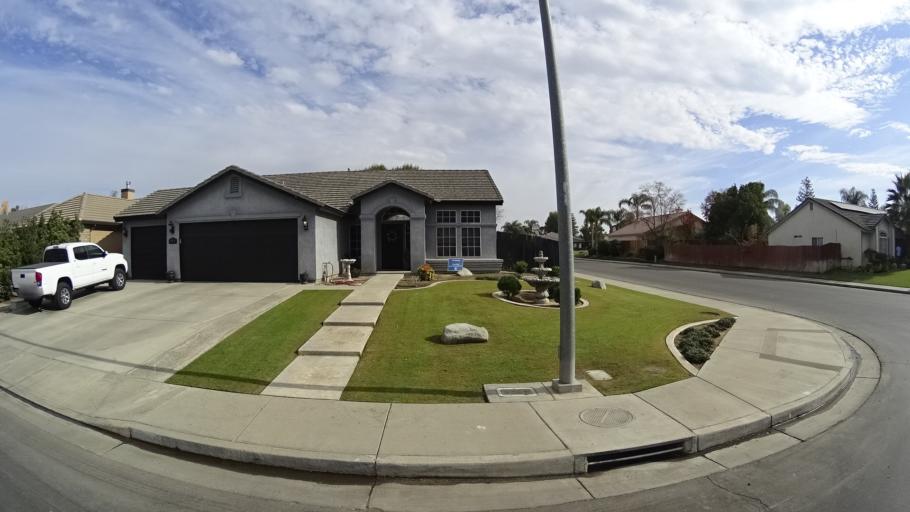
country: US
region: California
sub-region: Kern County
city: Greenacres
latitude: 35.4016
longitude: -119.1235
